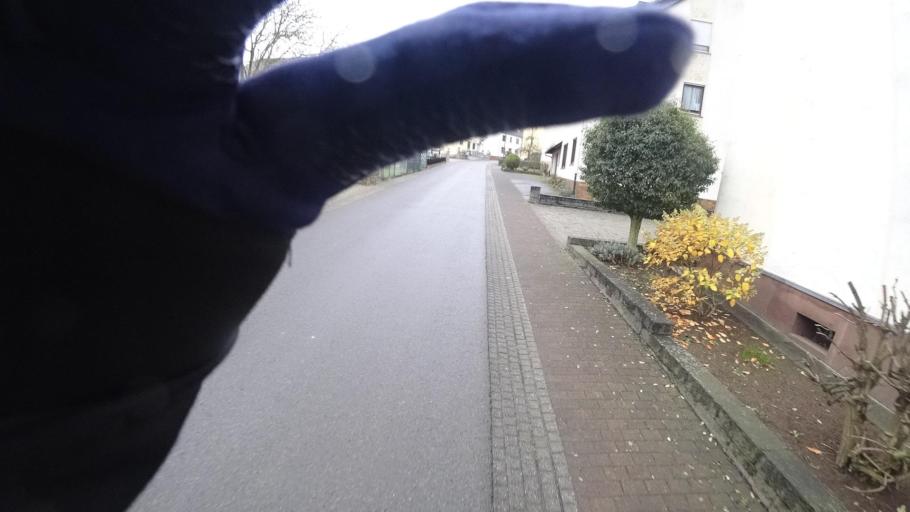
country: DE
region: Rheinland-Pfalz
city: Urbar
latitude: 50.1327
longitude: 7.7180
